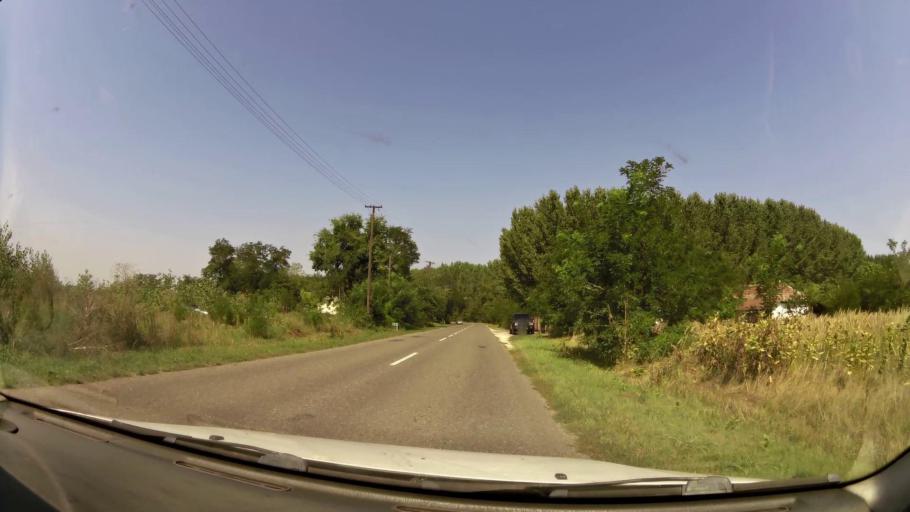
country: HU
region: Pest
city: Tapioszolos
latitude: 47.2799
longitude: 19.8785
